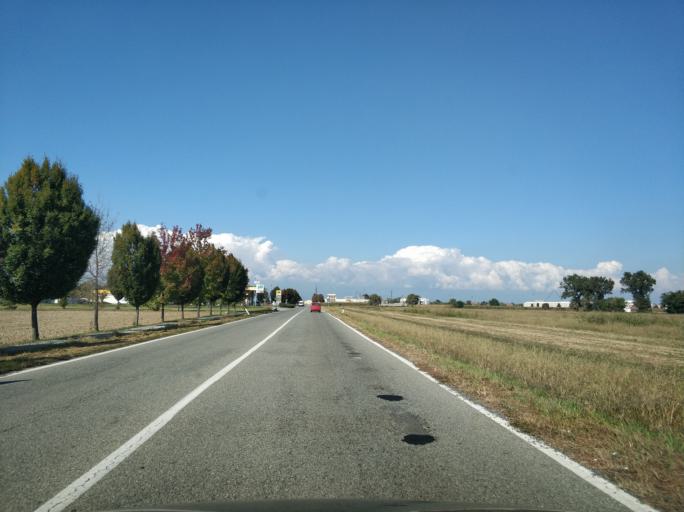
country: IT
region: Piedmont
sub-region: Provincia di Torino
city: Borgaro Torinese
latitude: 45.1448
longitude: 7.6787
